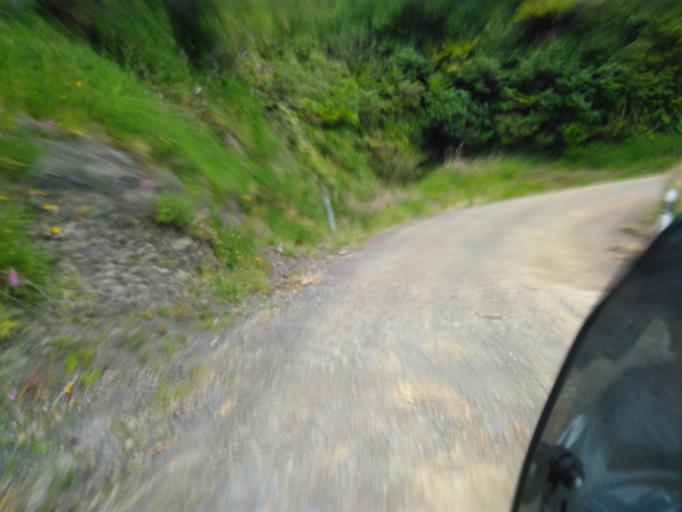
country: NZ
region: Bay of Plenty
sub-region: Opotiki District
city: Opotiki
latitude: -38.0949
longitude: 177.4855
